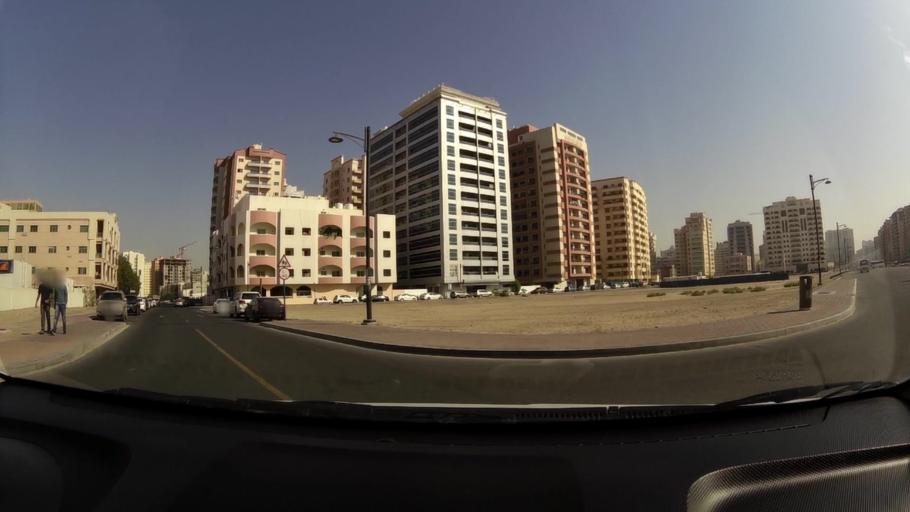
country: AE
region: Ash Shariqah
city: Sharjah
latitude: 25.2944
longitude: 55.3735
